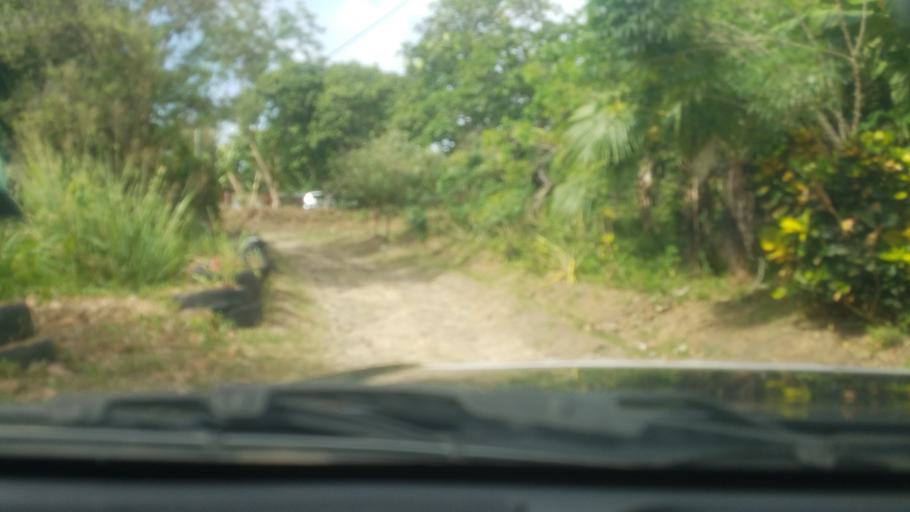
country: LC
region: Micoud Quarter
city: Micoud
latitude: 13.7990
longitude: -60.9183
